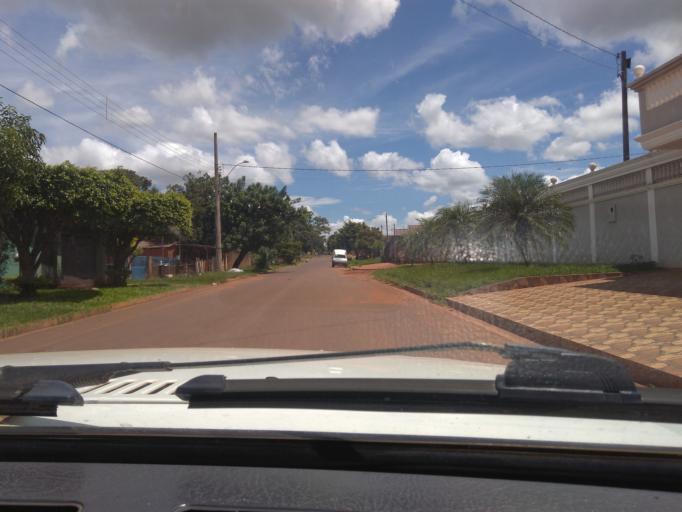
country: BR
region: Mato Grosso do Sul
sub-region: Ponta Pora
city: Ponta Pora
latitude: -22.5120
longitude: -55.7274
